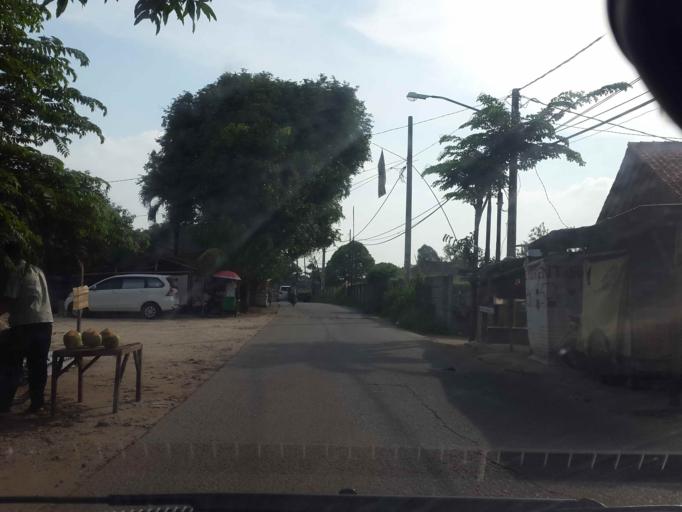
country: ID
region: West Java
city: Ciputat
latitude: -6.2642
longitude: 106.6732
